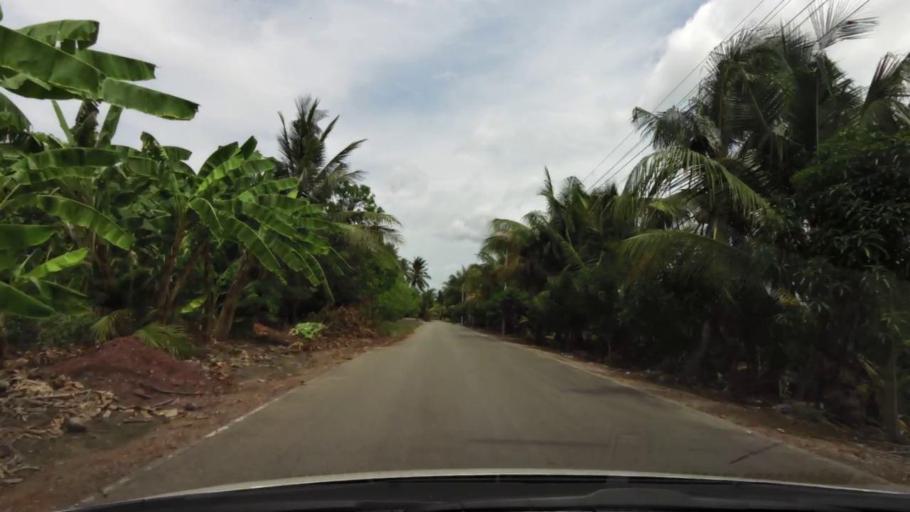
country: TH
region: Ratchaburi
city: Damnoen Saduak
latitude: 13.5144
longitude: 100.0093
